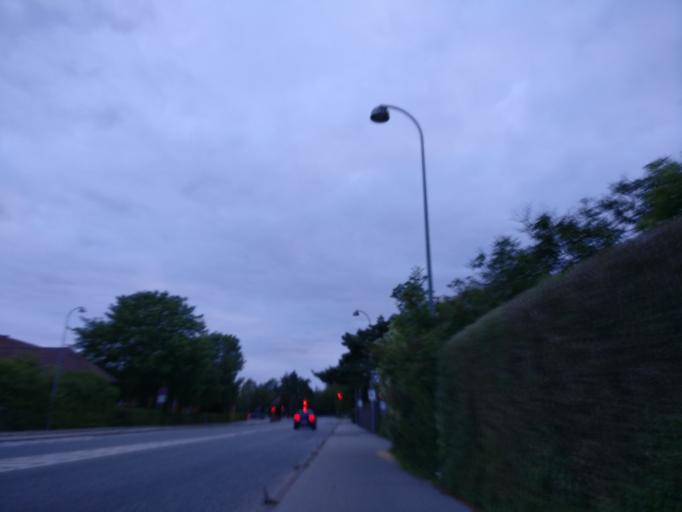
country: DK
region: Capital Region
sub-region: Hvidovre Kommune
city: Hvidovre
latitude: 55.6330
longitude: 12.4560
